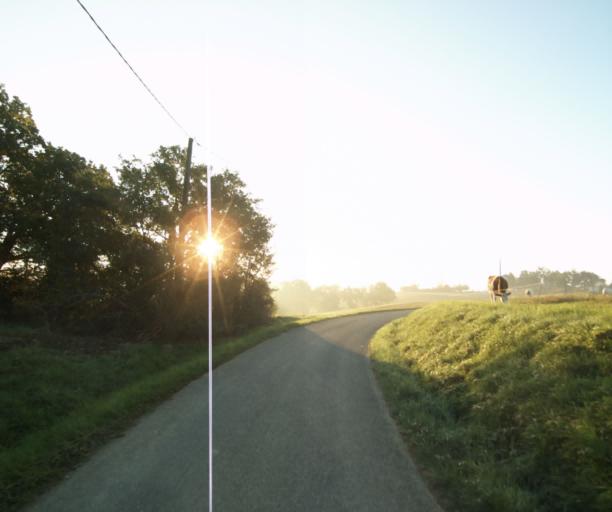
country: FR
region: Midi-Pyrenees
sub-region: Departement du Gers
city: Vic-Fezensac
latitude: 43.7711
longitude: 0.1921
